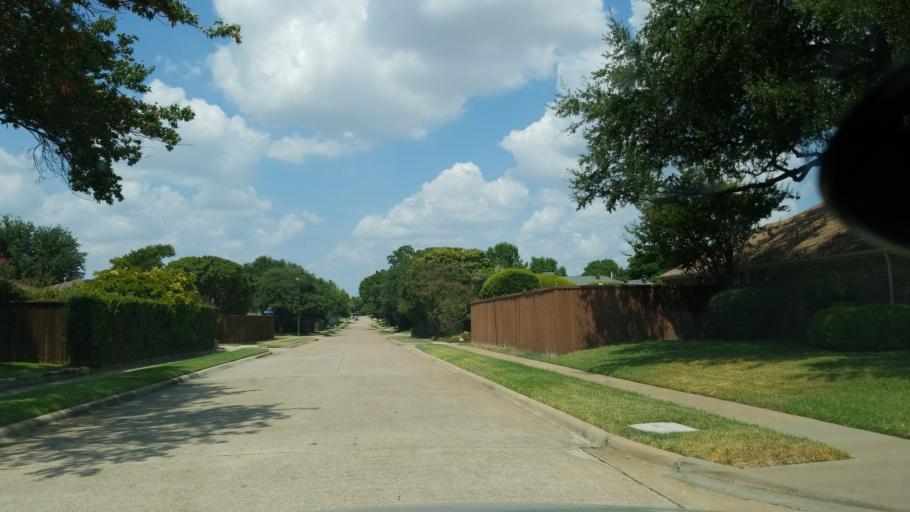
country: US
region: Texas
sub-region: Dallas County
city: Richardson
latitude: 32.9286
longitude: -96.7241
